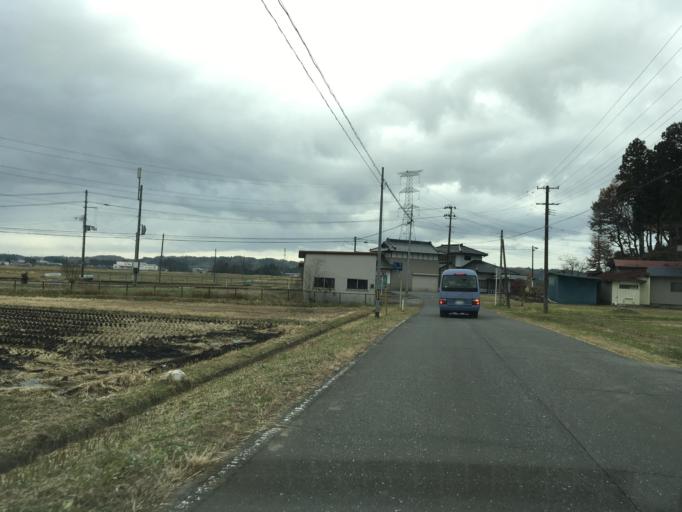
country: JP
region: Iwate
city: Ichinoseki
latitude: 38.8225
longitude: 141.0440
